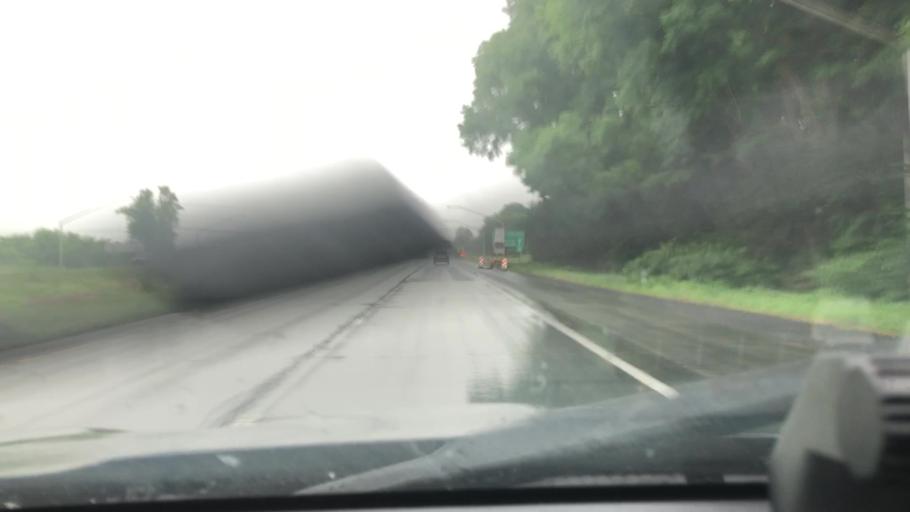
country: US
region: Pennsylvania
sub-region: Northampton County
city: Palmer Heights
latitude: 40.6970
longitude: -75.2896
